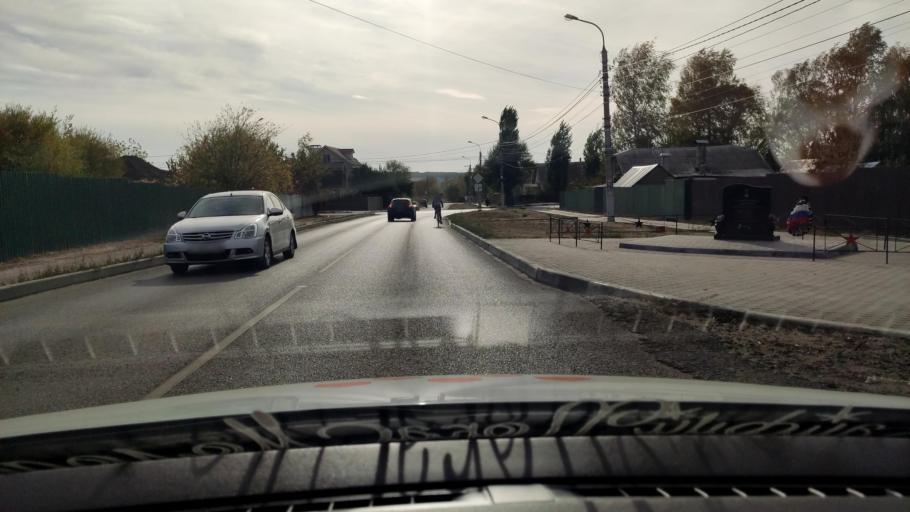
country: RU
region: Voronezj
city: Pridonskoy
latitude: 51.6817
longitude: 39.0757
